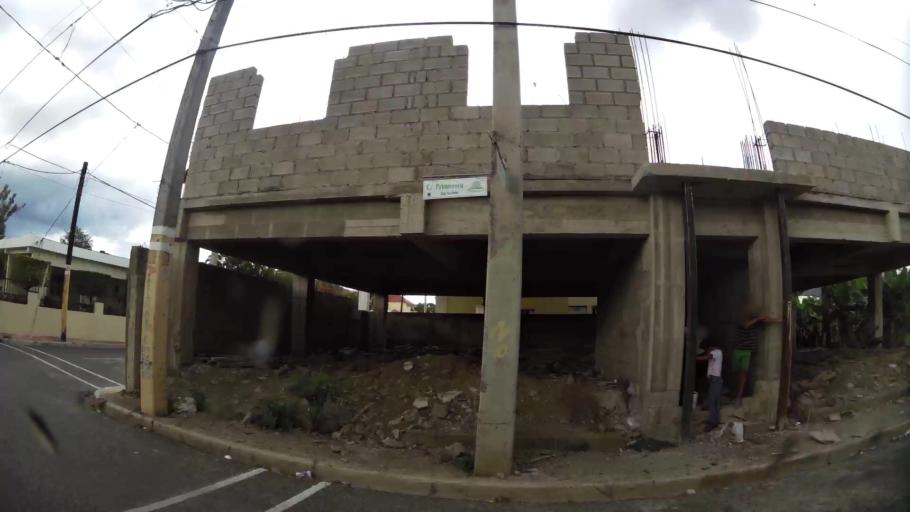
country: DO
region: Monsenor Nouel
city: Bonao
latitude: 18.9505
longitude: -70.4059
